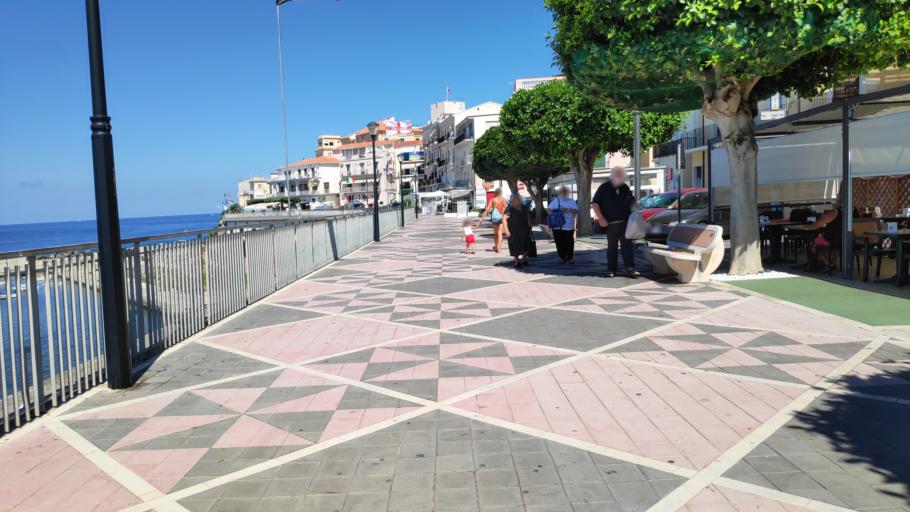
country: IT
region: Calabria
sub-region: Provincia di Cosenza
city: Diamante
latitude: 39.6771
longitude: 15.8184
